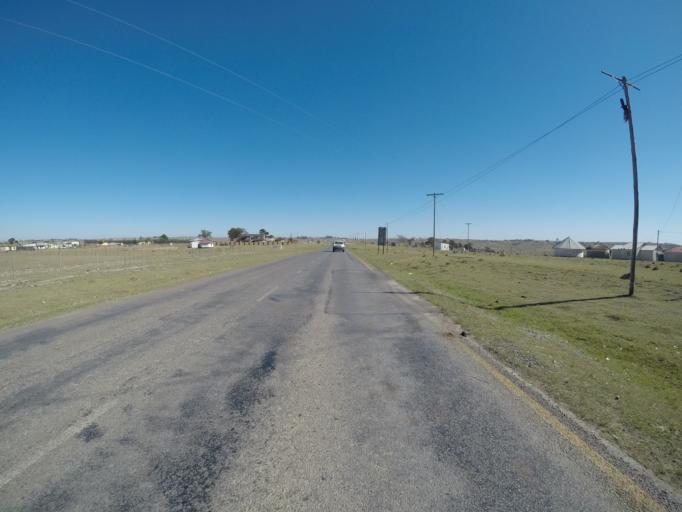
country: ZA
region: Eastern Cape
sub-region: OR Tambo District Municipality
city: Mthatha
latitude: -31.7854
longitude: 28.7416
